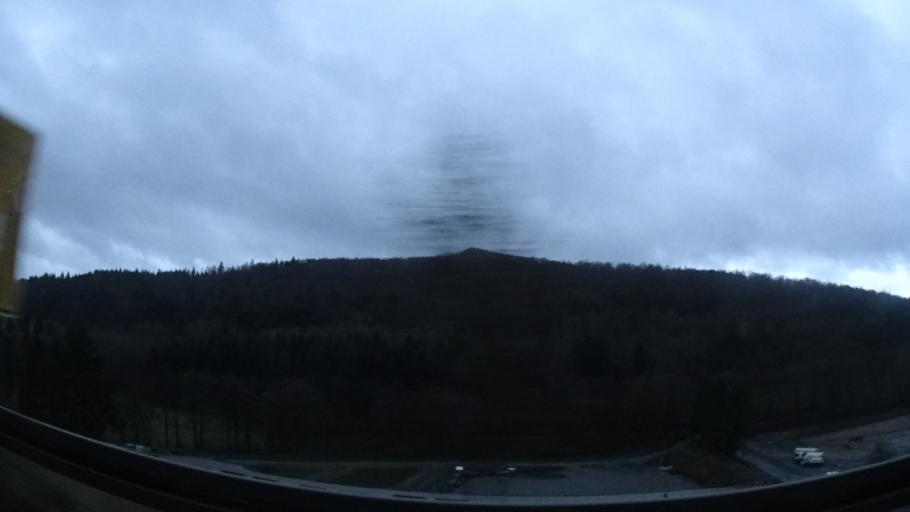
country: DE
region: Hesse
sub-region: Regierungsbezirk Kassel
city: Gersfeld
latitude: 50.4565
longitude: 9.8897
